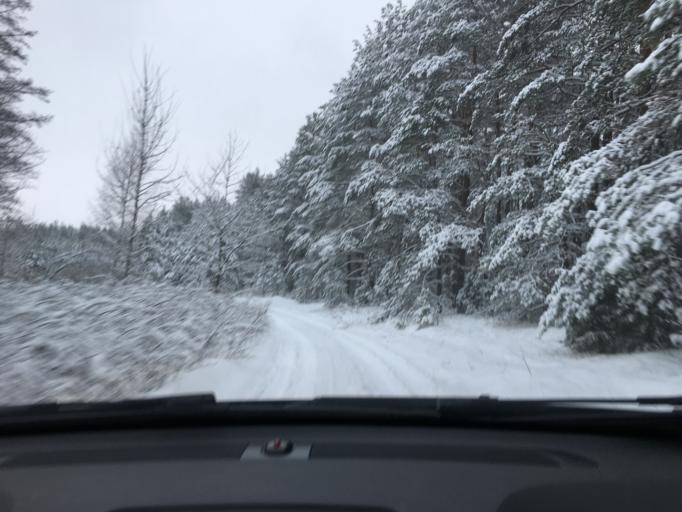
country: LT
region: Alytaus apskritis
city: Druskininkai
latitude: 53.9184
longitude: 24.1940
